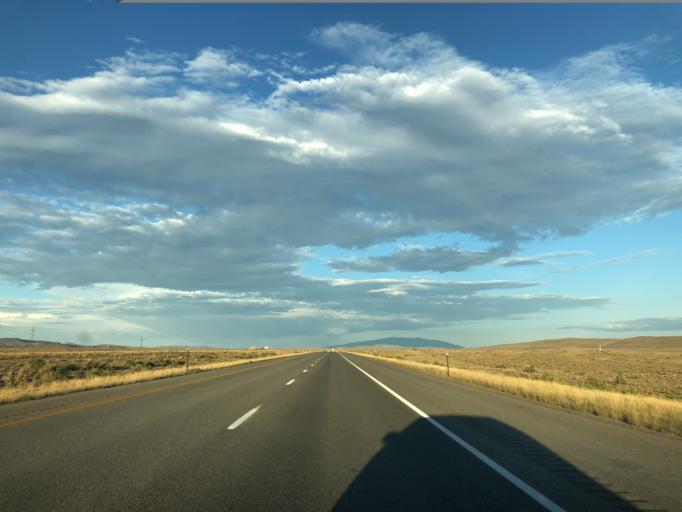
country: US
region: Wyoming
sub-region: Carbon County
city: Rawlins
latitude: 41.7662
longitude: -107.0309
